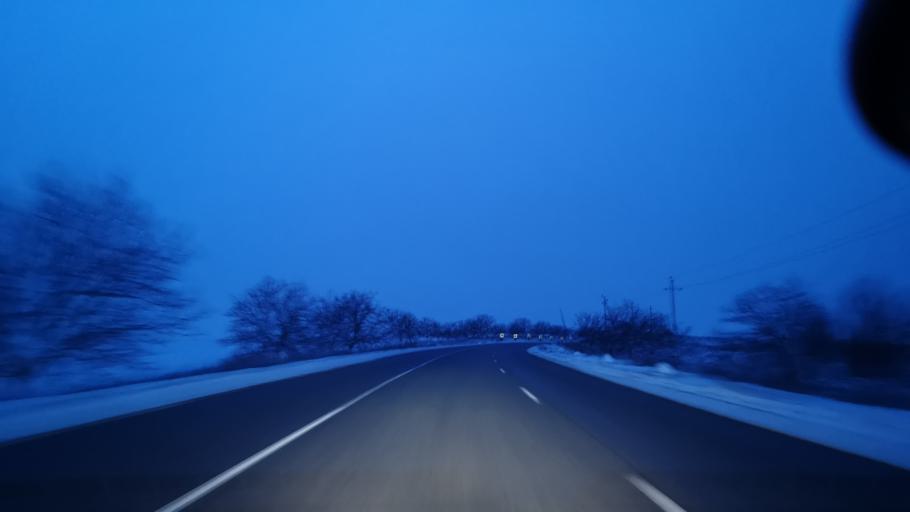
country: MD
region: Rezina
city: Saharna
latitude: 47.5876
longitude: 28.8197
